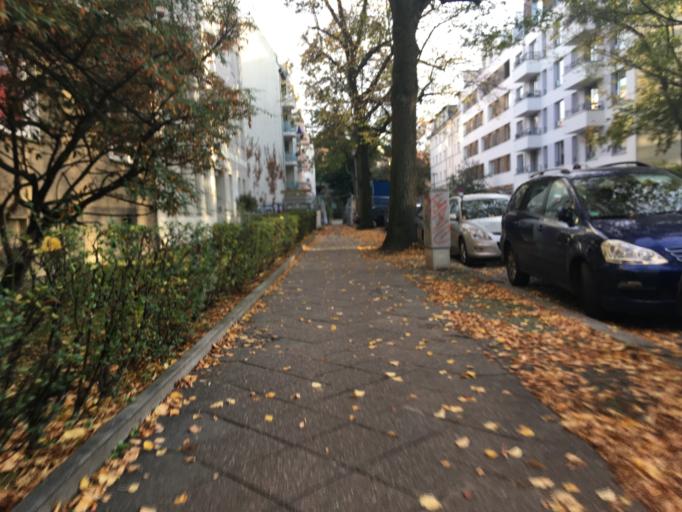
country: DE
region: Berlin
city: Pankow
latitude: 52.5636
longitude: 13.3985
